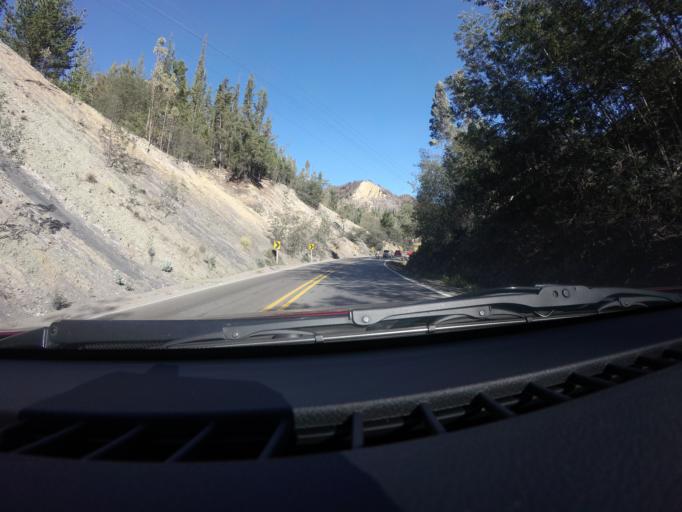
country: CO
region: Cundinamarca
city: Sutatausa
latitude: 5.2472
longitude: -73.8551
